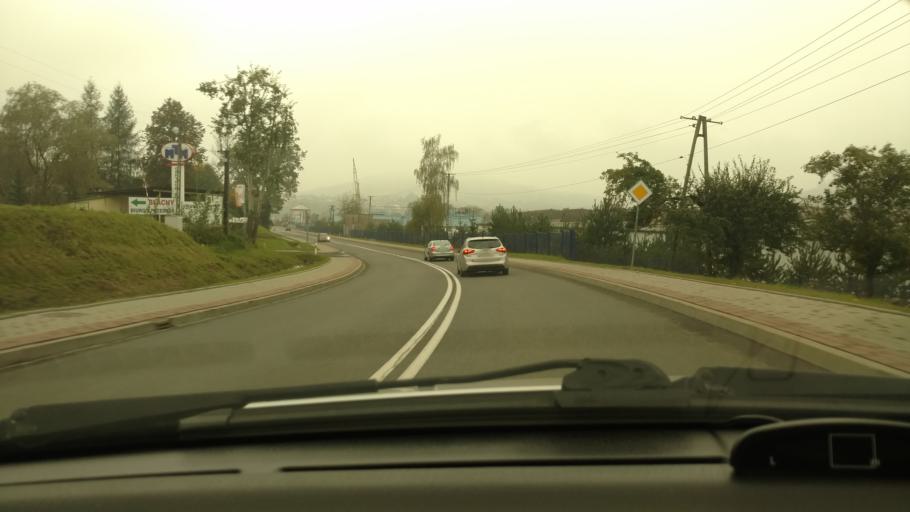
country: PL
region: Lesser Poland Voivodeship
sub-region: Powiat nowosadecki
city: Grybow
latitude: 49.6265
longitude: 20.9596
